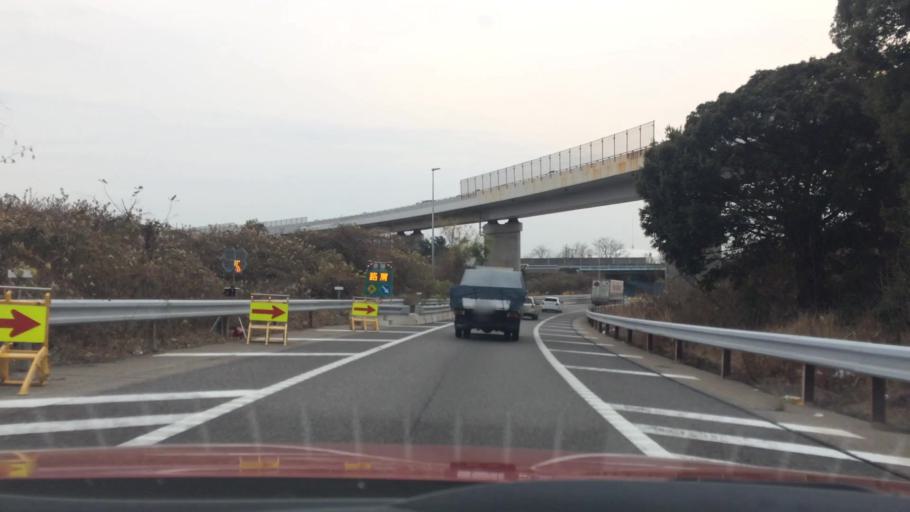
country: JP
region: Aichi
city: Kasugai
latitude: 35.2864
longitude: 136.9801
